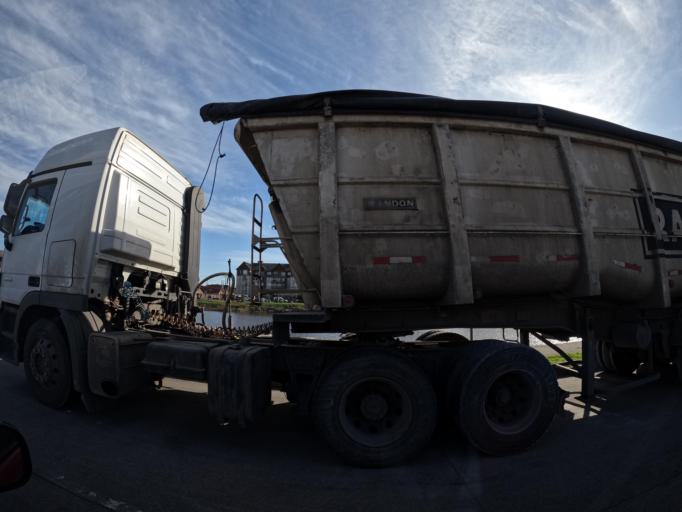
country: CL
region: Biobio
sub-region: Provincia de Concepcion
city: Talcahuano
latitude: -36.7689
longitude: -73.0748
